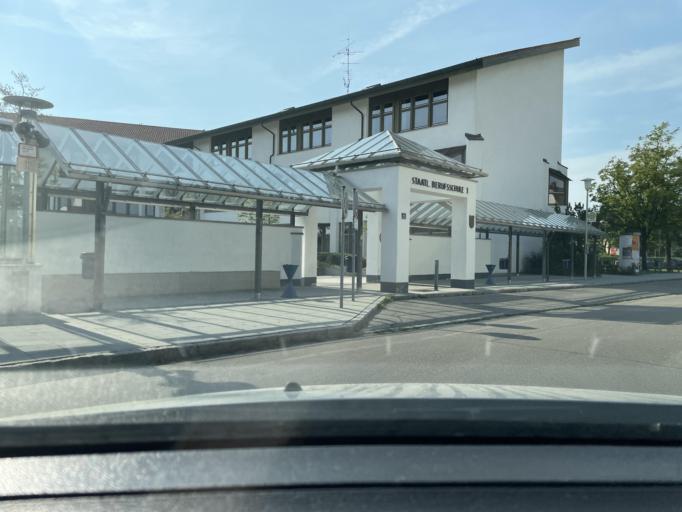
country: DE
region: Bavaria
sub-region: Upper Bavaria
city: Muehldorf
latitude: 48.2459
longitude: 12.5271
